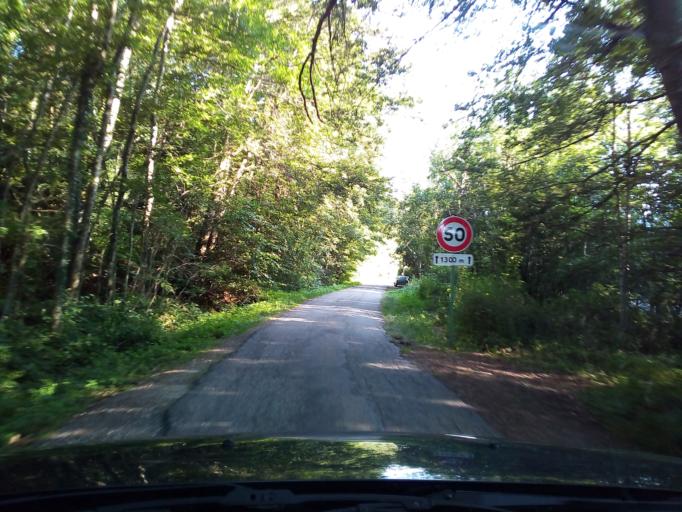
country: FR
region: Rhone-Alpes
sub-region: Departement de l'Isere
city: Notre-Dame-de-Mesage
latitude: 45.0138
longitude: 5.7861
